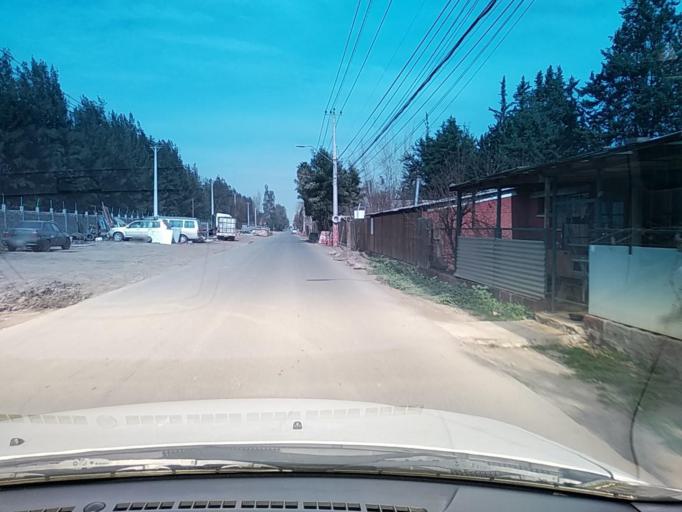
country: CL
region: Santiago Metropolitan
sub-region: Provincia de Chacabuco
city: Chicureo Abajo
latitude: -33.2895
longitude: -70.7273
